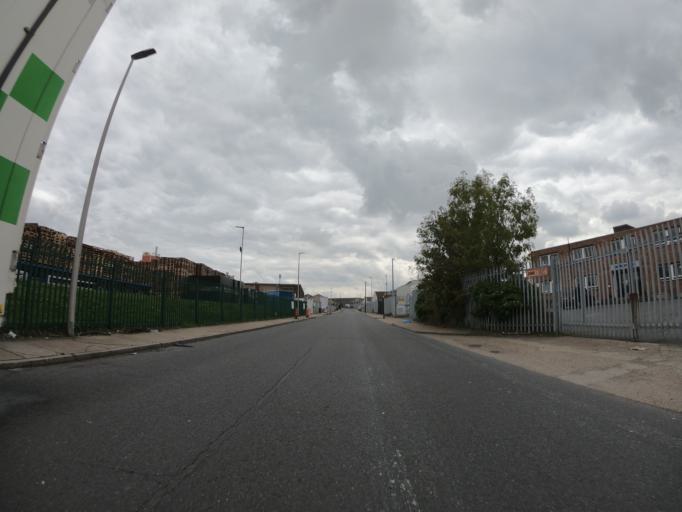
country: GB
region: England
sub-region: Greater London
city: Belvedere
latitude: 51.5004
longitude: 0.1650
